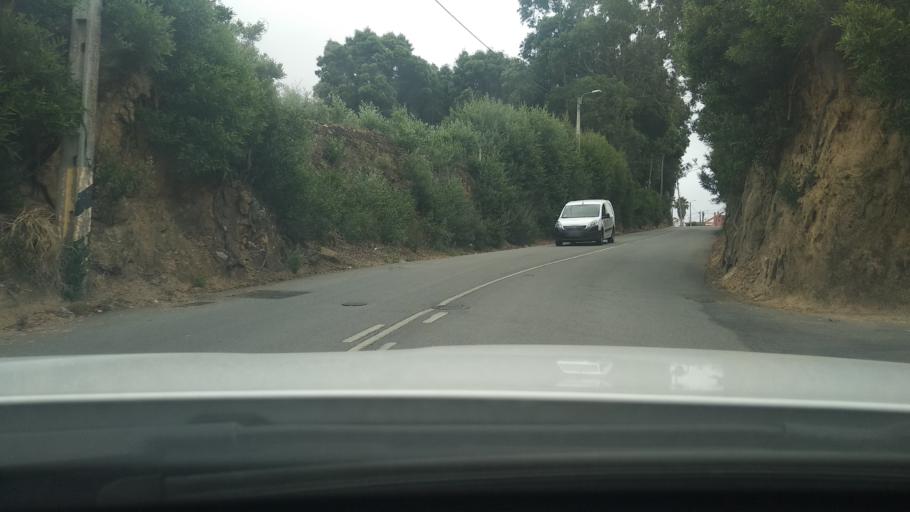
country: PT
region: Aveiro
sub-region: Espinho
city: Silvalde
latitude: 40.9962
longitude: -8.6268
